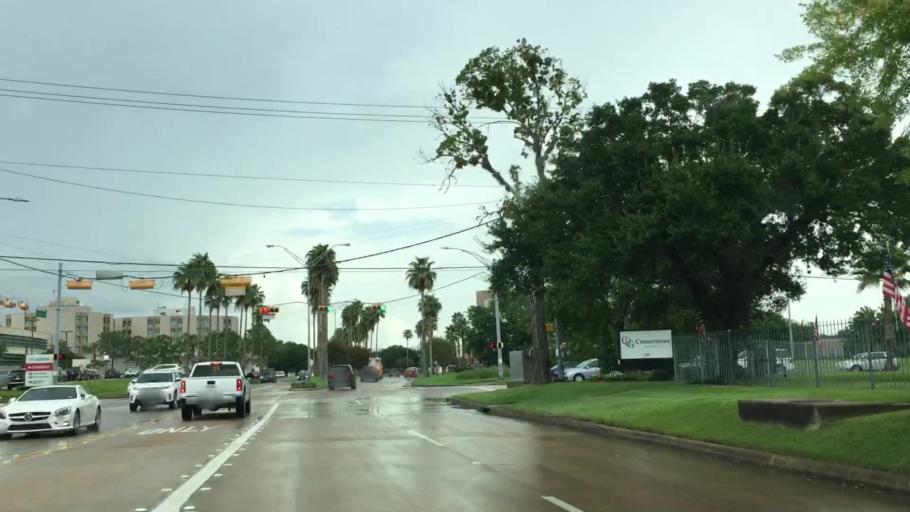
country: US
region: Texas
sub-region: Harris County
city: Webster
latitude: 29.5385
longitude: -95.1299
